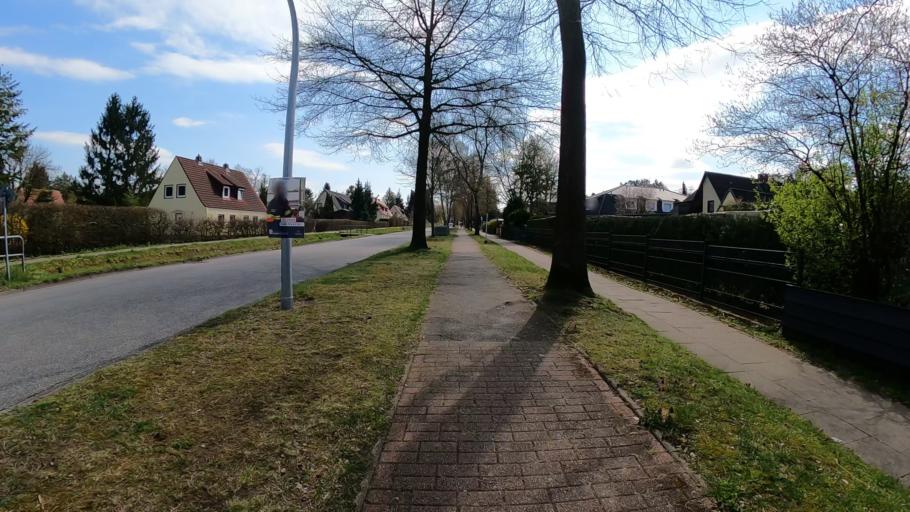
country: DE
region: Lower Saxony
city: Neu Wulmstorf
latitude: 53.4563
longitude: 9.8666
